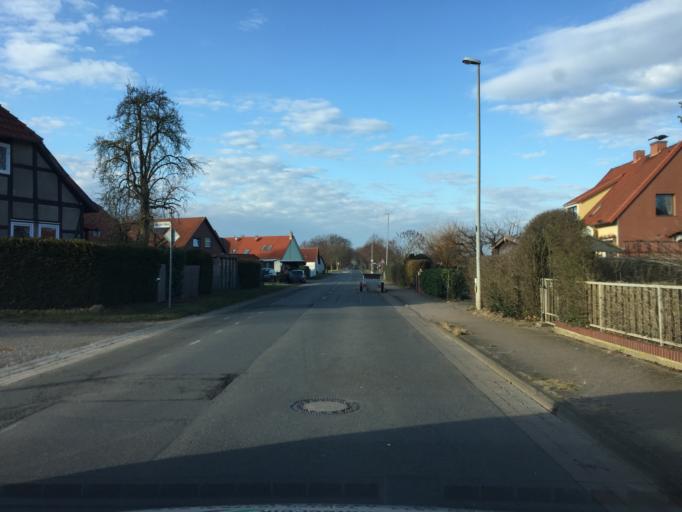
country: DE
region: Lower Saxony
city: Garbsen
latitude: 52.4444
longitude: 9.5312
